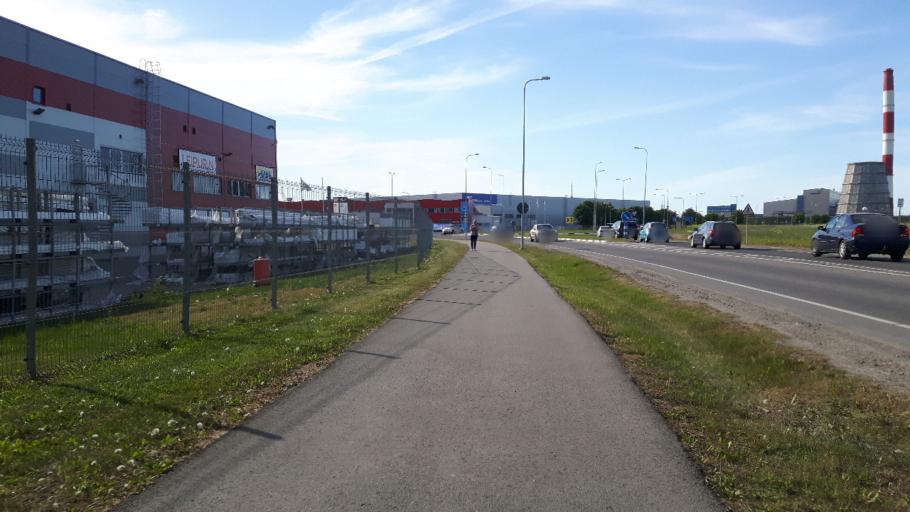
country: EE
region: Harju
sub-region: Joelaehtme vald
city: Loo
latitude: 59.4422
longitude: 24.9316
